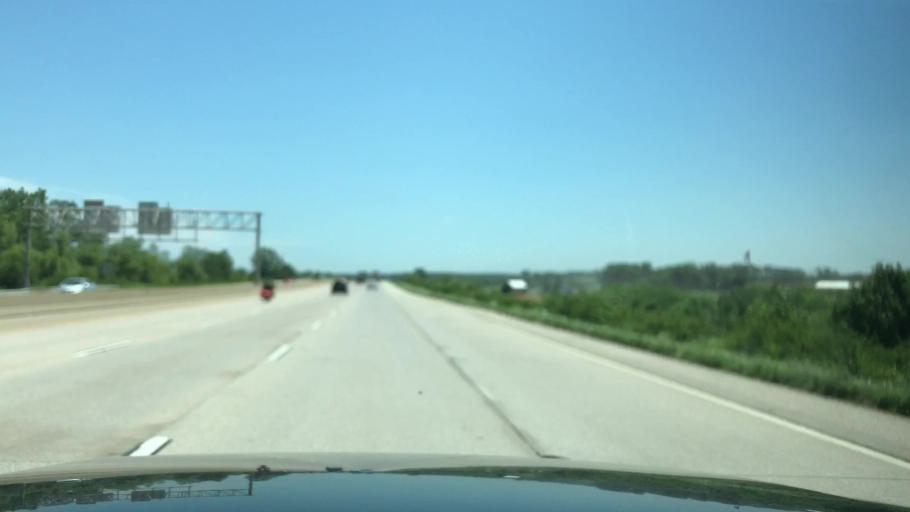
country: US
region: Missouri
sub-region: Saint Charles County
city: Saint Charles
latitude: 38.7918
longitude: -90.4483
